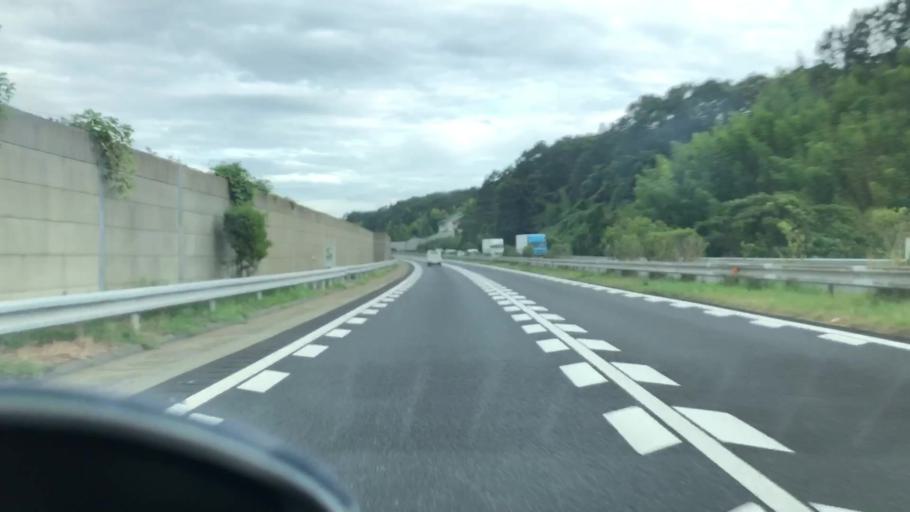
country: JP
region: Hyogo
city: Yashiro
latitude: 34.9007
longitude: 135.0698
